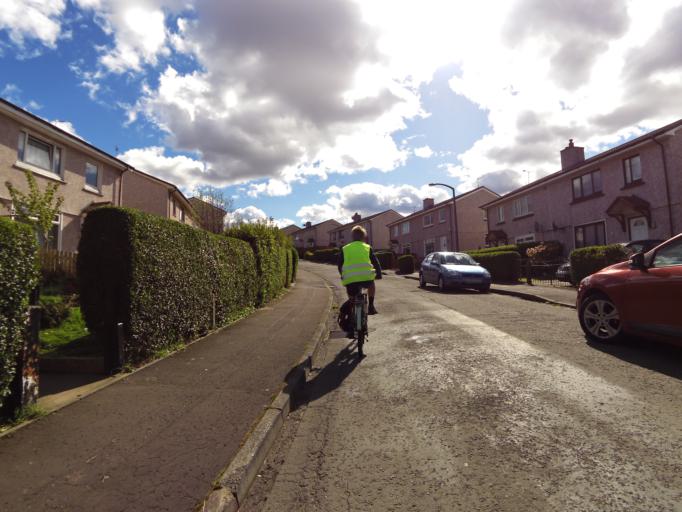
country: GB
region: Scotland
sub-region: Midlothian
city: Loanhead
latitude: 55.9159
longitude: -3.1366
